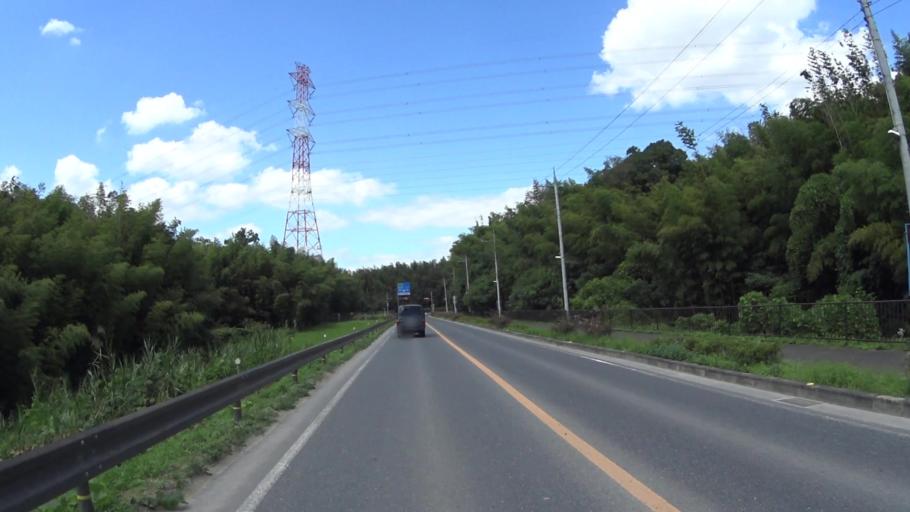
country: JP
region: Kyoto
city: Tanabe
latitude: 34.8467
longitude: 135.7903
